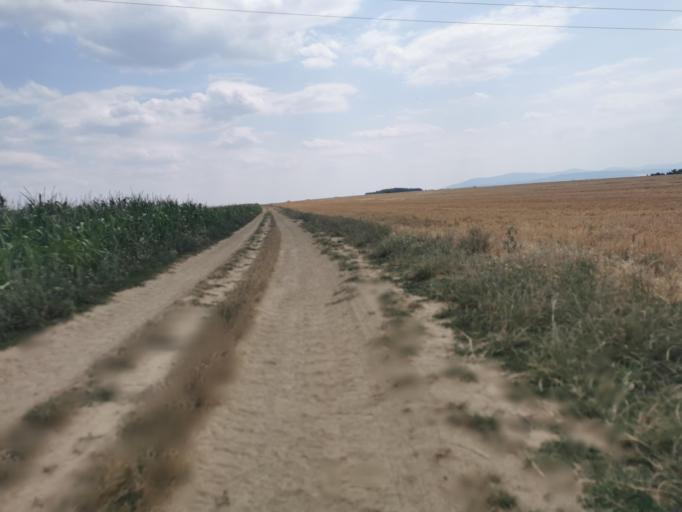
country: SK
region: Trnavsky
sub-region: Okres Senica
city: Senica
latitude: 48.6848
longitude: 17.4240
